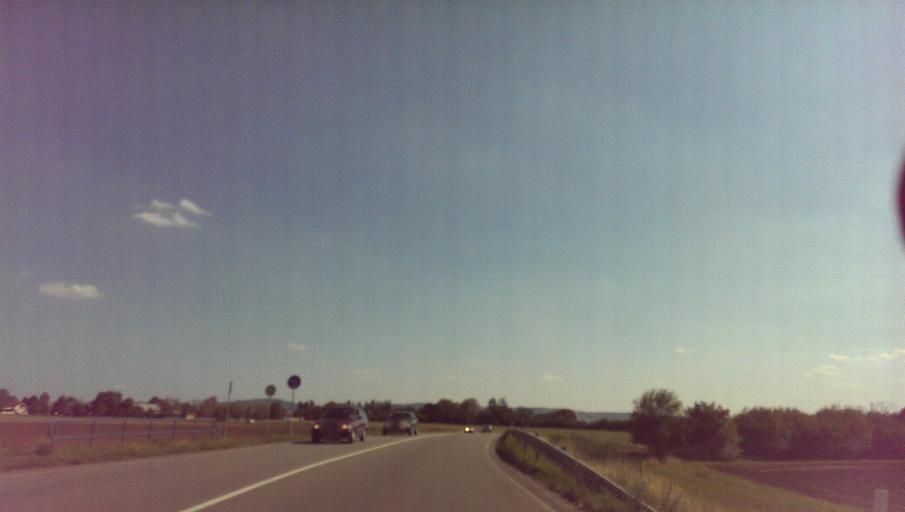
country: CZ
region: Zlin
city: Holesov
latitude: 49.3149
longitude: 17.5949
